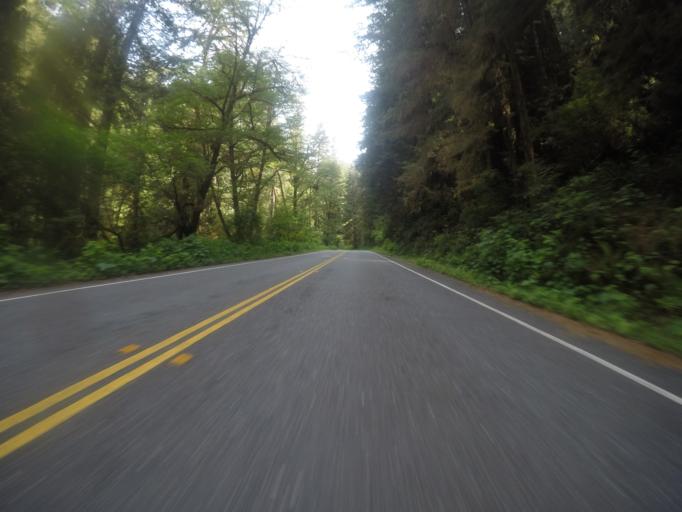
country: US
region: California
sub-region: Del Norte County
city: Bertsch-Oceanview
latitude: 41.4321
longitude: -124.0385
